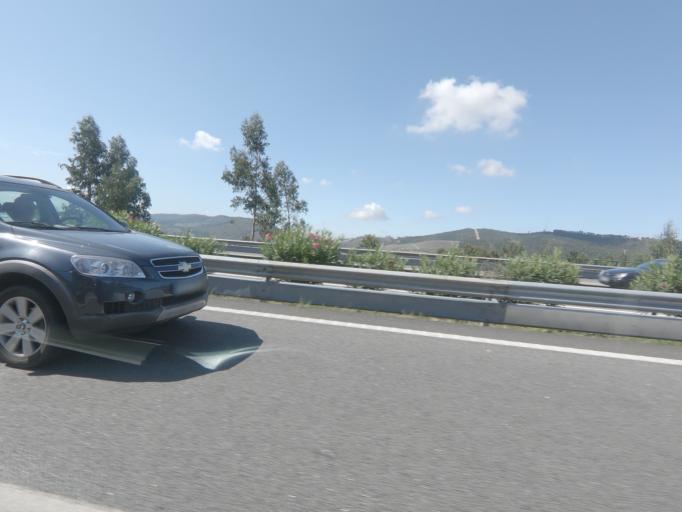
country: PT
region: Porto
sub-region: Valongo
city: Campo
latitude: 41.1885
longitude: -8.4771
